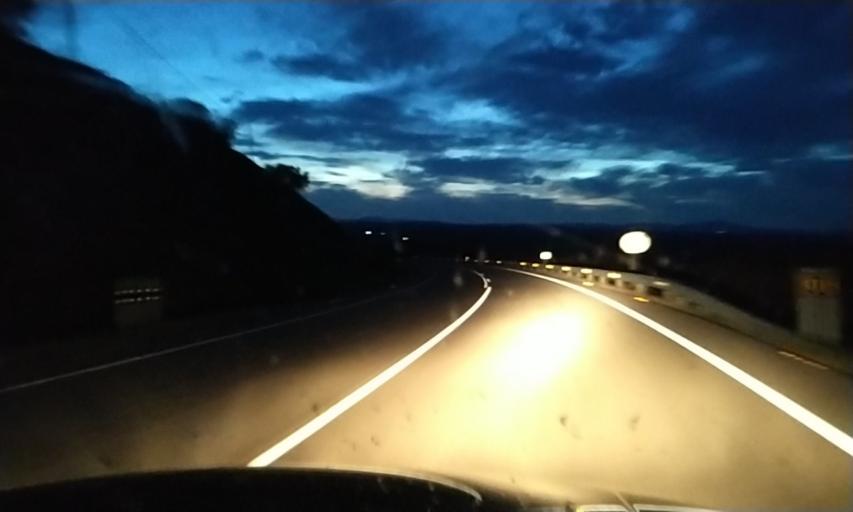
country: ES
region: Extremadura
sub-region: Provincia de Caceres
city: Galisteo
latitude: 39.9784
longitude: -6.2041
